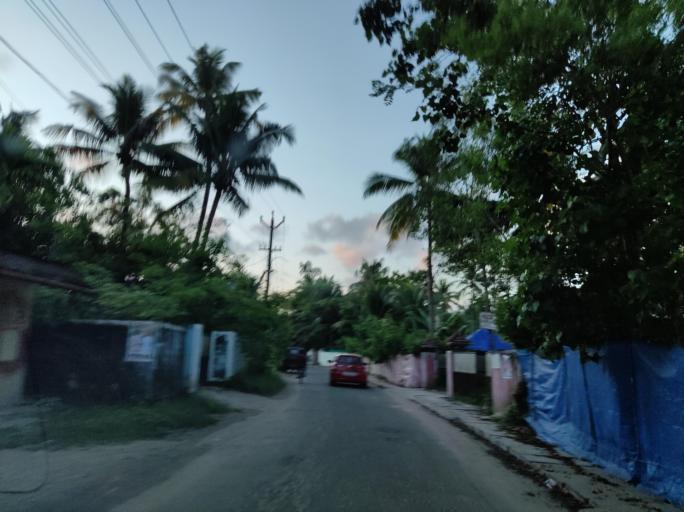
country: IN
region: Kerala
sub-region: Alappuzha
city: Vayalar
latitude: 9.7437
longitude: 76.2871
